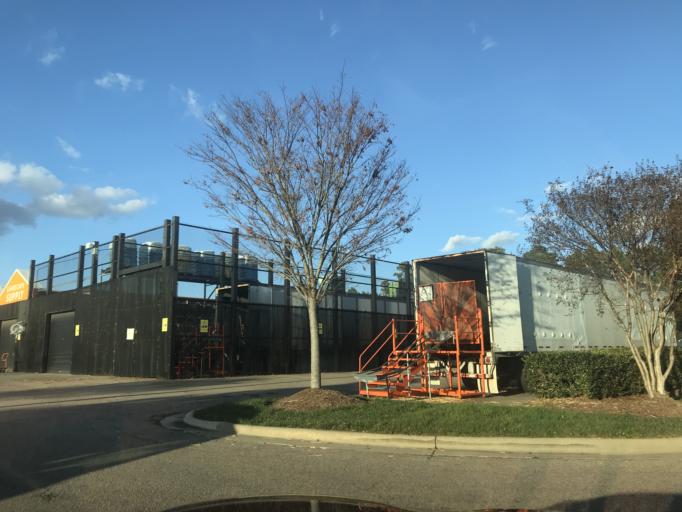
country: US
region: North Carolina
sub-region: Wake County
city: Knightdale
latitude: 35.7982
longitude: -78.5045
